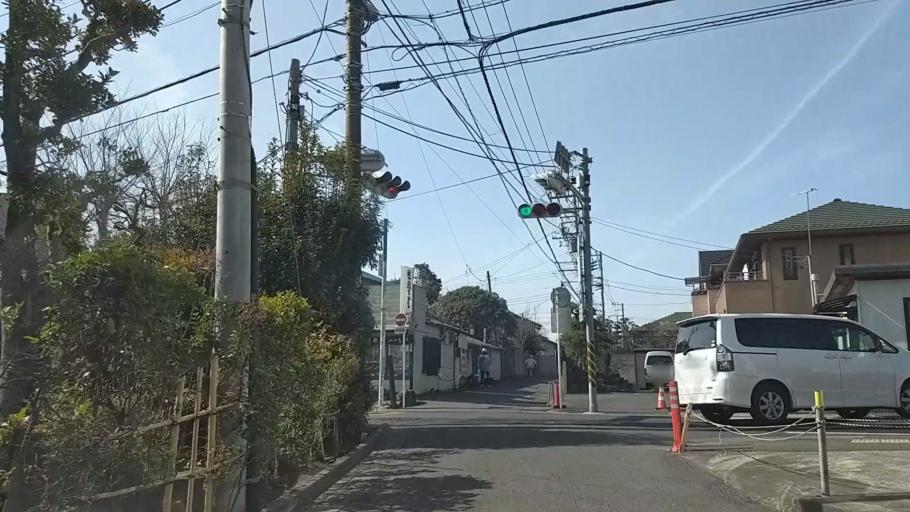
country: JP
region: Kanagawa
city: Chigasaki
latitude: 35.3491
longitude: 139.4143
